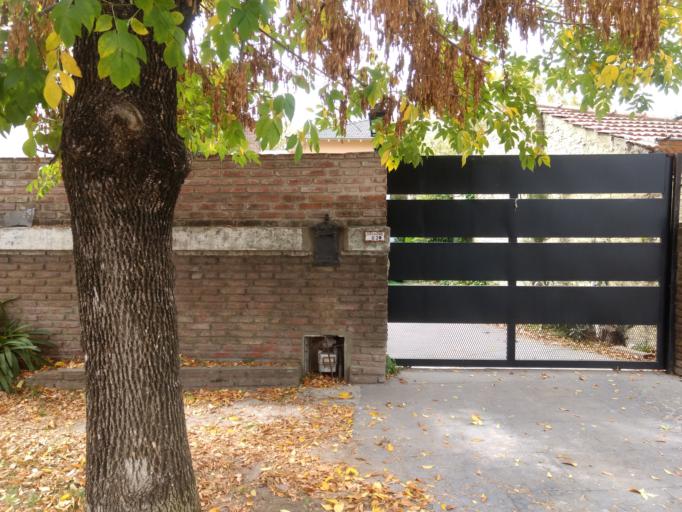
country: AR
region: Buenos Aires
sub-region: Partido de Florencio Varela
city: Florencio Varela
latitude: -34.8181
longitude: -58.4546
